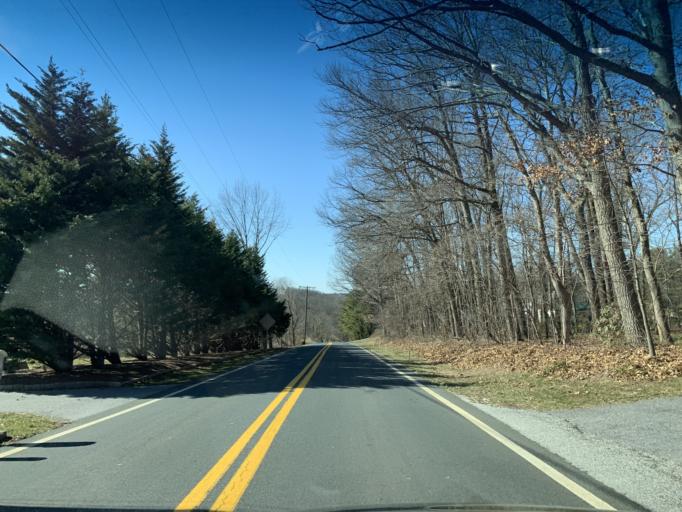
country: US
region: Maryland
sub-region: Carroll County
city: Hampstead
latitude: 39.5732
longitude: -76.8808
